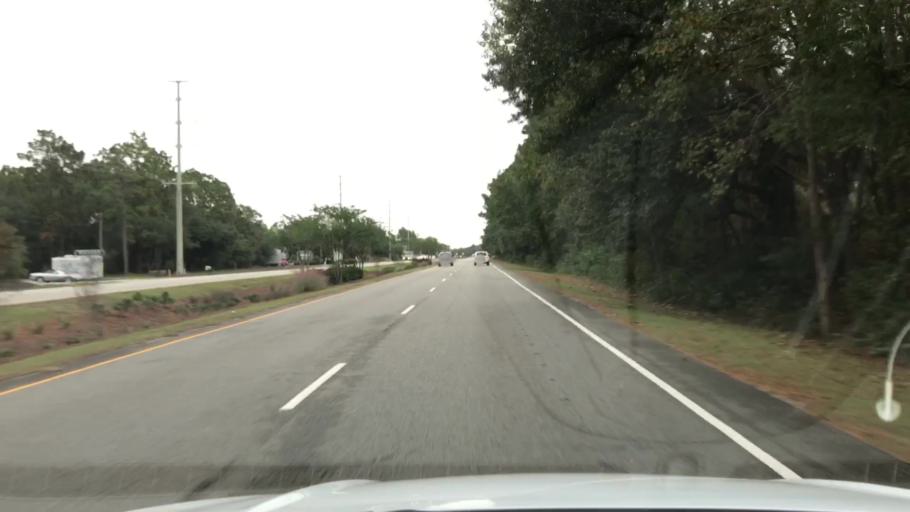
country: US
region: South Carolina
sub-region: Georgetown County
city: Georgetown
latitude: 33.4238
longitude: -79.1639
